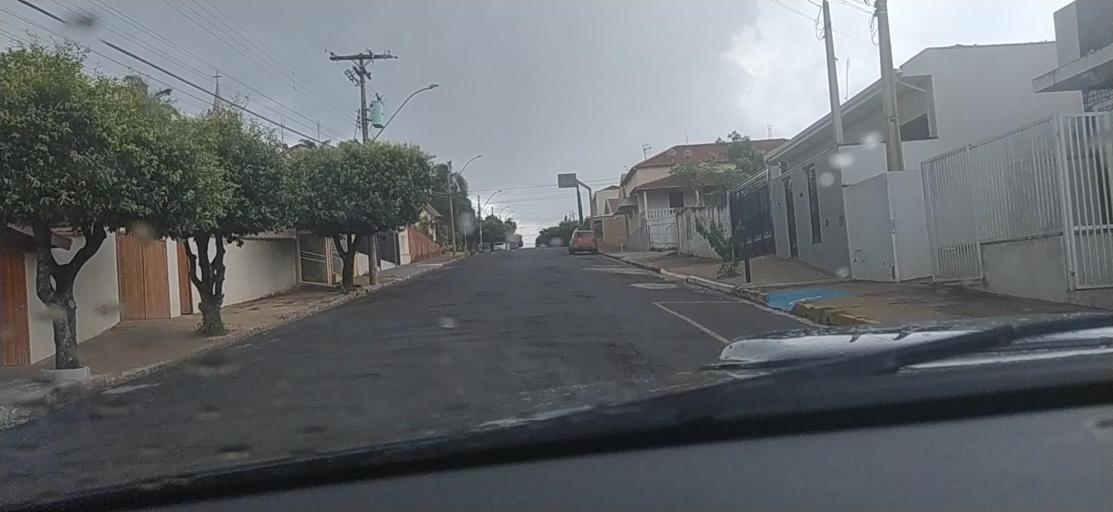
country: BR
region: Sao Paulo
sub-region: Pindorama
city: Pindorama
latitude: -21.1864
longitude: -48.9068
